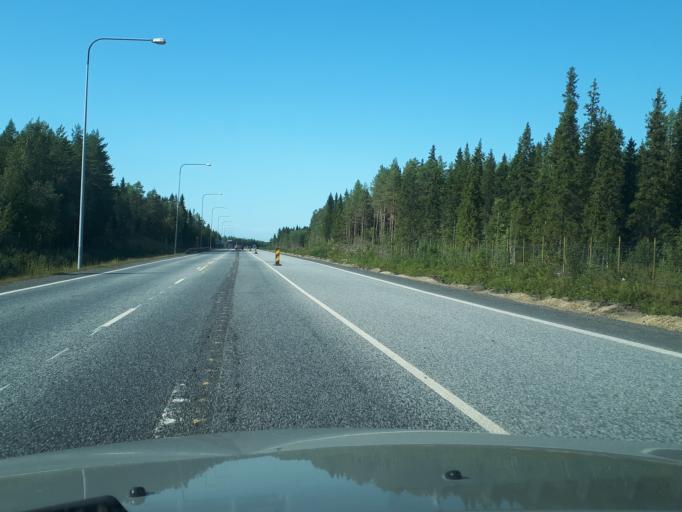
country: FI
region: Northern Ostrobothnia
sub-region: Oulunkaari
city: Ii
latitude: 65.2572
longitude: 25.3717
